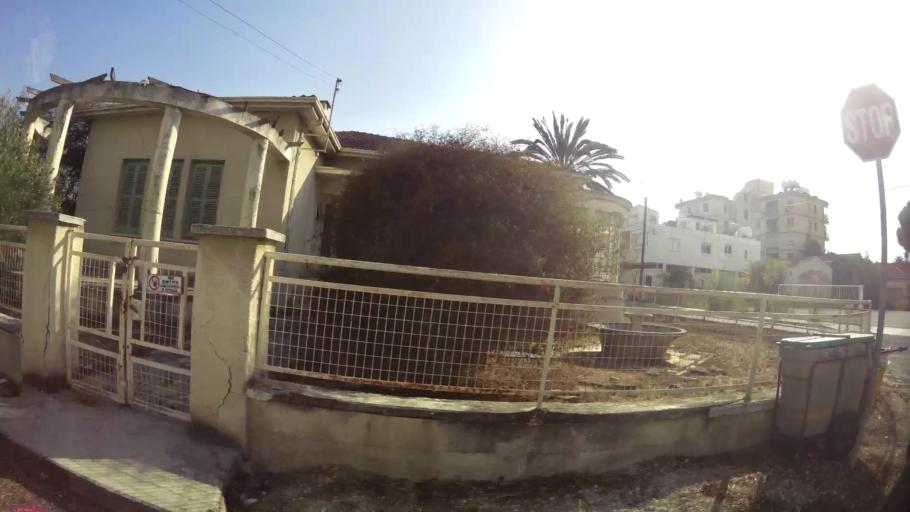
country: CY
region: Lefkosia
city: Nicosia
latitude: 35.1762
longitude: 33.3444
